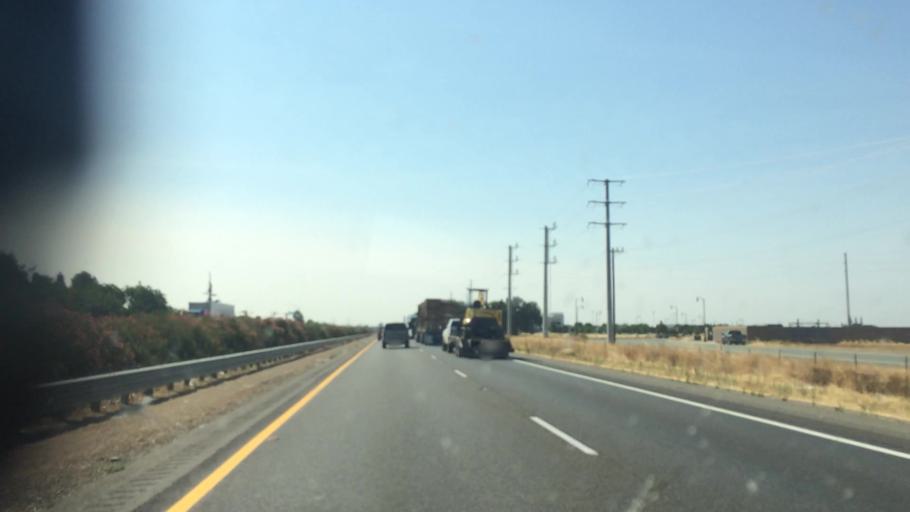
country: US
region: California
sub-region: Sacramento County
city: Elk Grove
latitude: 38.3885
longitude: -121.3740
